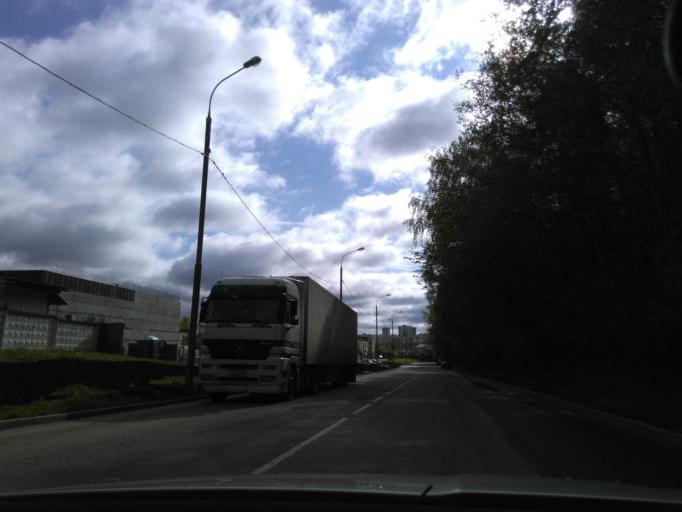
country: RU
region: Moscow
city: Zelenograd
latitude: 56.0052
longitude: 37.1801
